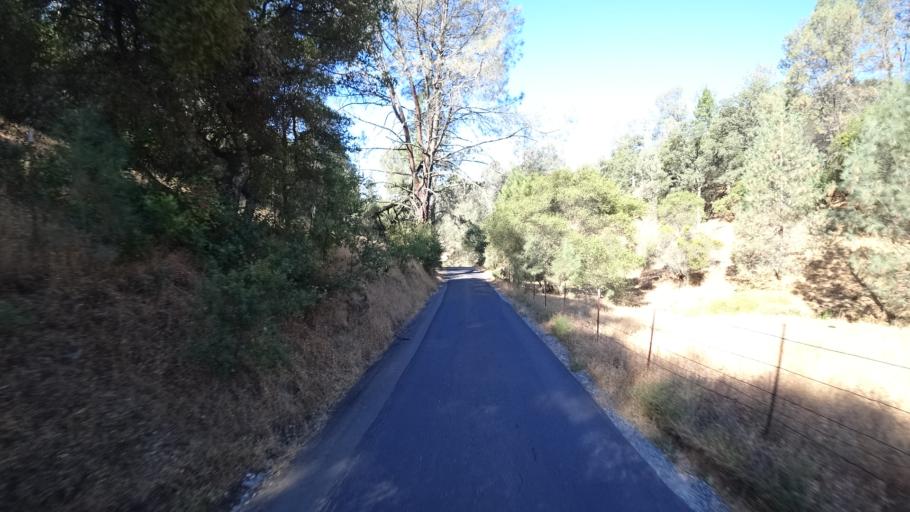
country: US
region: California
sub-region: Calaveras County
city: San Andreas
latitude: 38.2293
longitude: -120.6694
